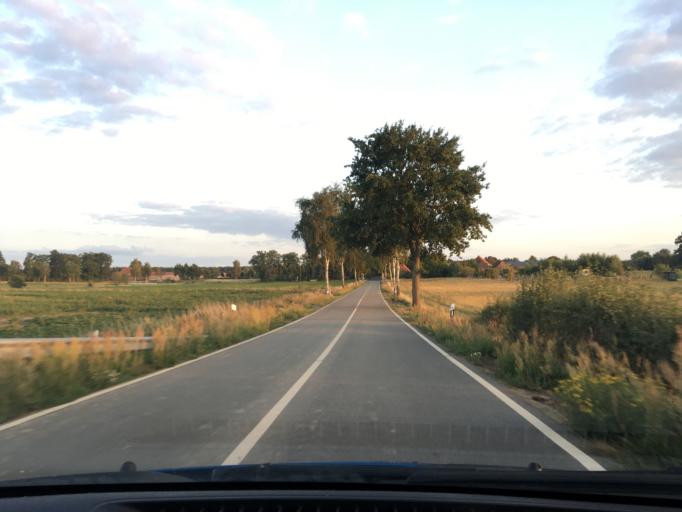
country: DE
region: Lower Saxony
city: Nahrendorf
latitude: 53.1630
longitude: 10.8094
